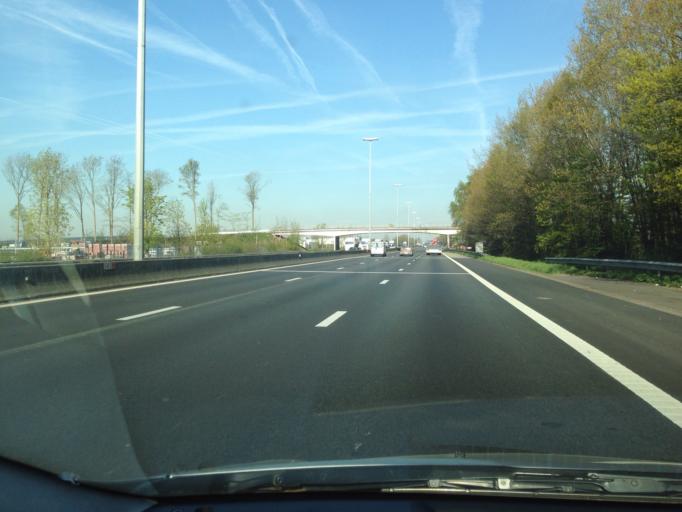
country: BE
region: Flanders
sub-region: Provincie Oost-Vlaanderen
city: Nevele
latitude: 51.0463
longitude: 3.5897
